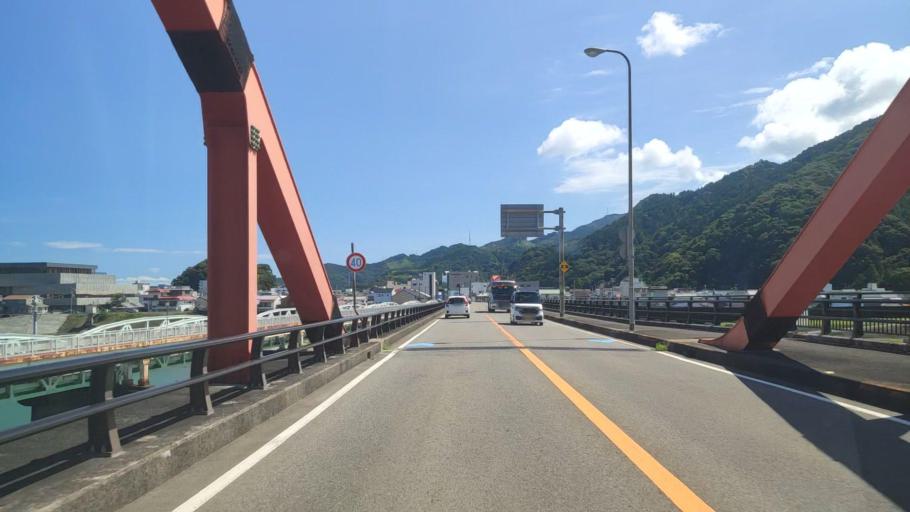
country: JP
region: Wakayama
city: Shingu
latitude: 33.7336
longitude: 135.9878
